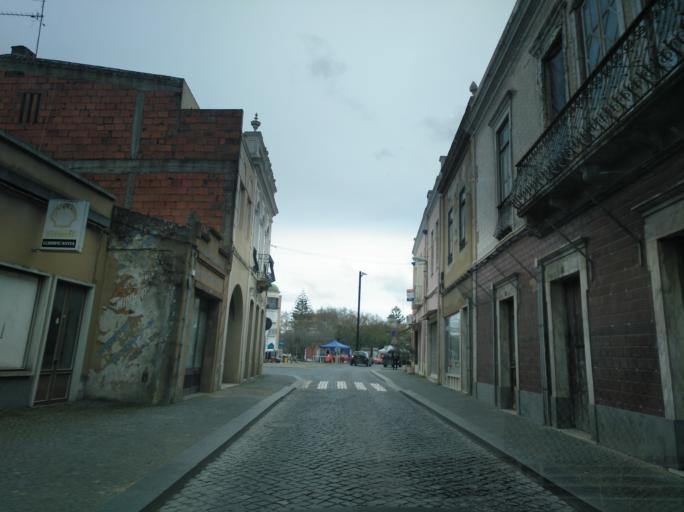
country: PT
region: Setubal
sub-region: Grandola
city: Grandola
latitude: 38.1763
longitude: -8.5665
